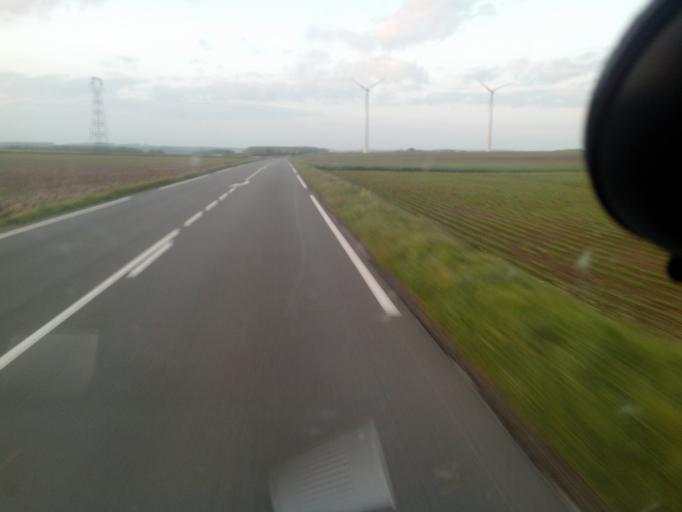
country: FR
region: Picardie
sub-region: Departement de la Somme
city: Crecy-en-Ponthieu
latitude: 50.2443
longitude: 1.9558
